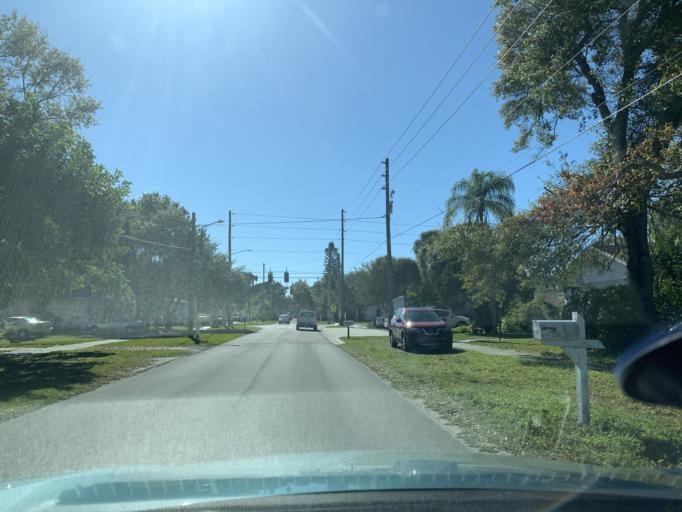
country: US
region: Florida
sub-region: Pinellas County
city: Gulfport
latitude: 27.7490
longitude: -82.7038
